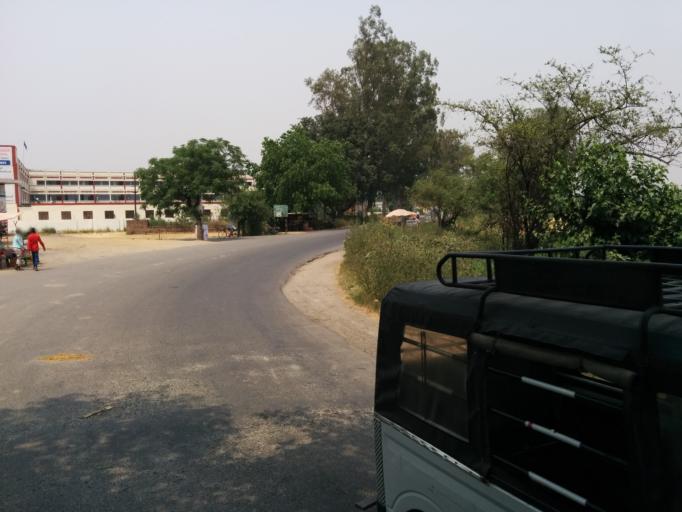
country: IN
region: Punjab
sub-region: Gurdaspur
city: Dhariwal
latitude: 31.9359
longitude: 75.3072
